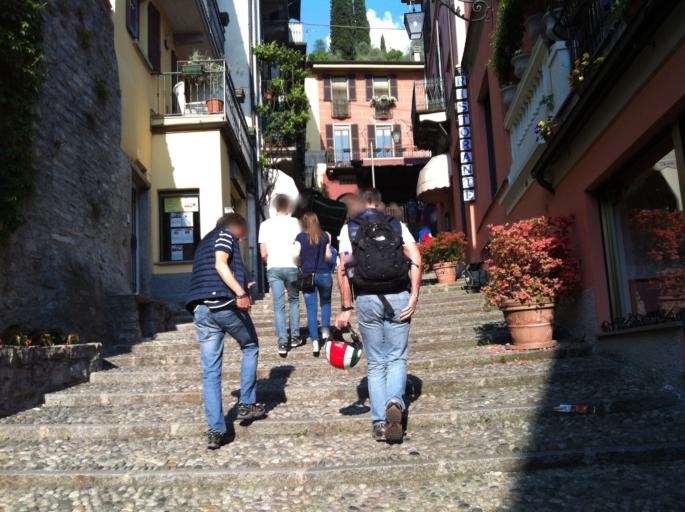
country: IT
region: Lombardy
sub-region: Provincia di Como
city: Bellagio
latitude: 45.9866
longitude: 9.2619
